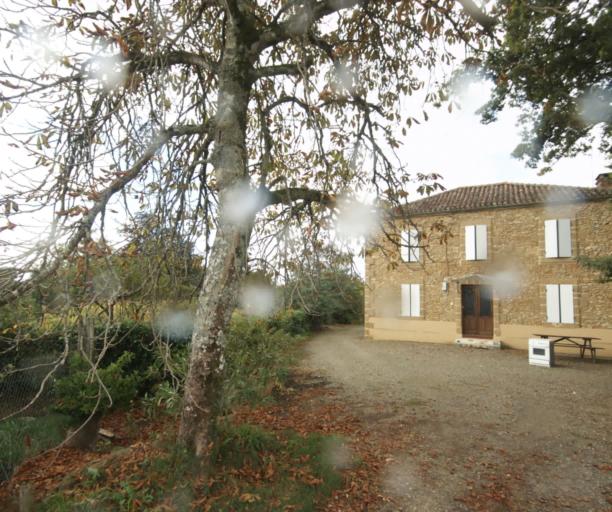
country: FR
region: Midi-Pyrenees
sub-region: Departement du Gers
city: Nogaro
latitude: 43.8300
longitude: -0.0867
